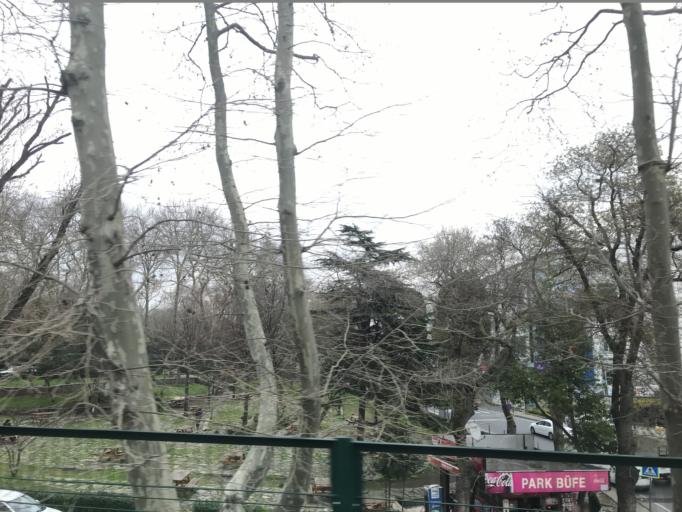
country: TR
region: Istanbul
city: Bahcelievler
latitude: 40.9726
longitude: 28.7894
